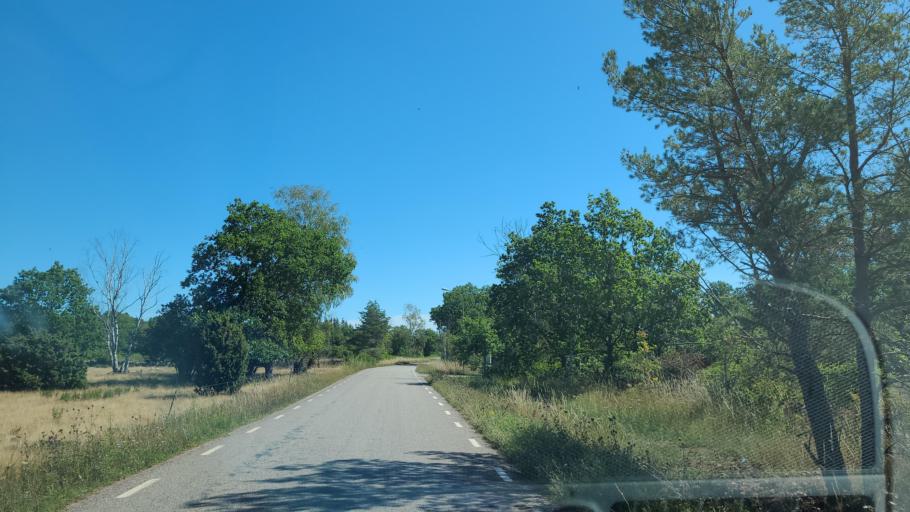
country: SE
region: Kalmar
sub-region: Borgholms Kommun
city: Borgholm
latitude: 56.7685
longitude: 16.6320
